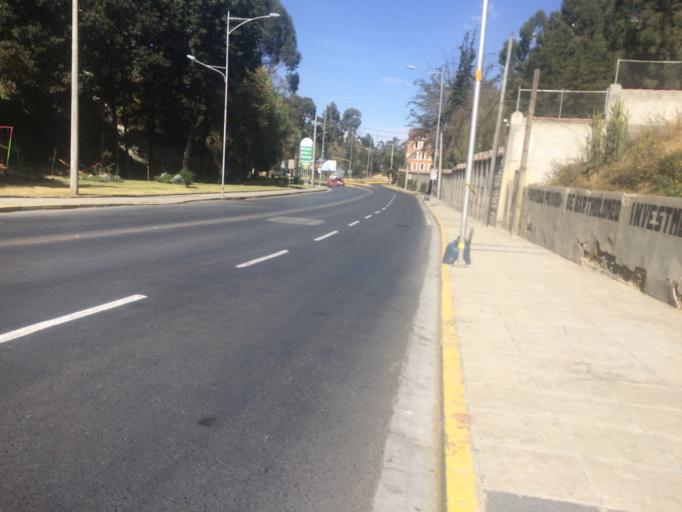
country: BO
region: La Paz
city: La Paz
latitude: -16.5110
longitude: -68.1208
